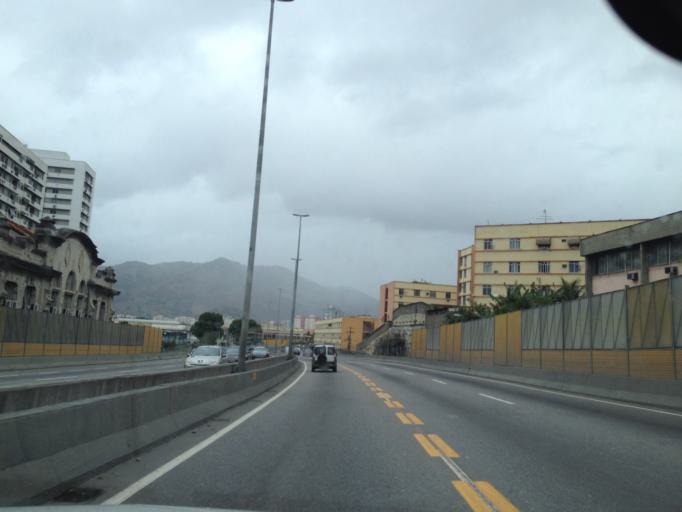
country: BR
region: Rio de Janeiro
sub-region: Rio De Janeiro
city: Rio de Janeiro
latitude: -22.8846
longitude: -43.2909
